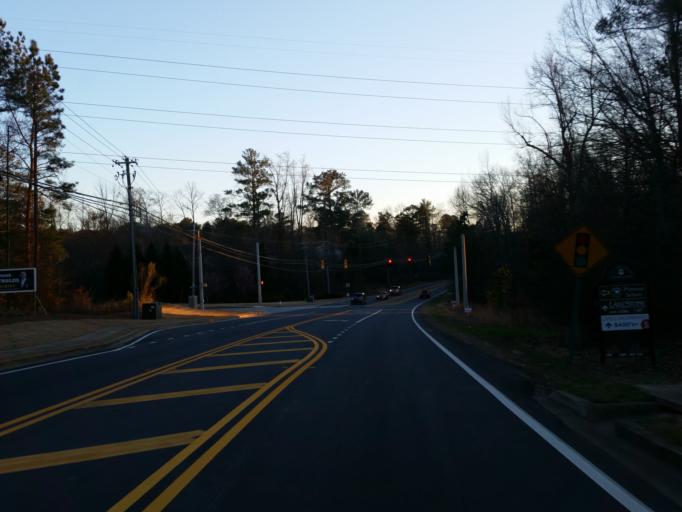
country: US
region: Georgia
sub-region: Cherokee County
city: Woodstock
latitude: 34.0996
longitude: -84.4704
